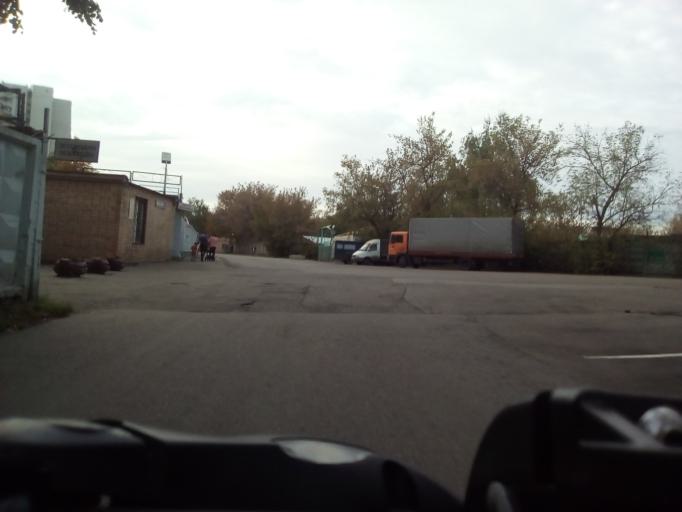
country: RU
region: Moscow
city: Leonovo
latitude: 55.8375
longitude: 37.6488
